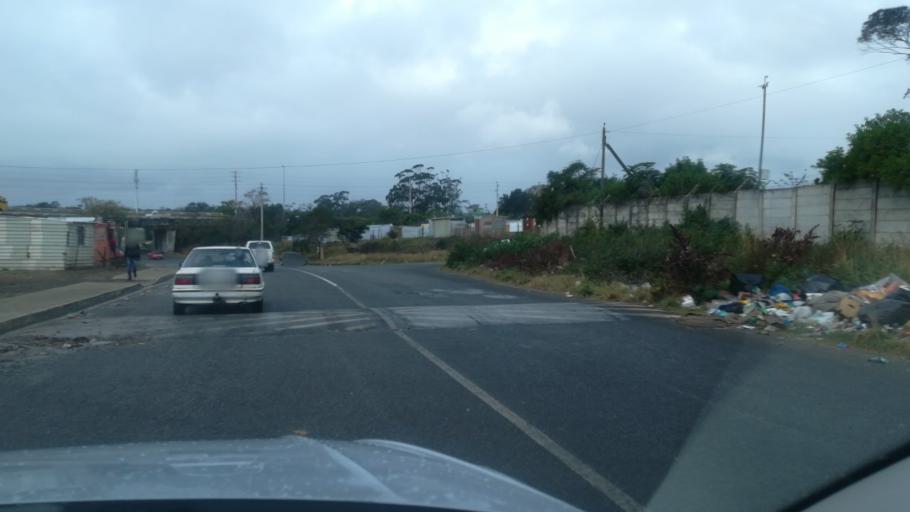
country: ZA
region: Eastern Cape
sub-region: Buffalo City Metropolitan Municipality
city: East London
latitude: -33.0009
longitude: 27.8399
